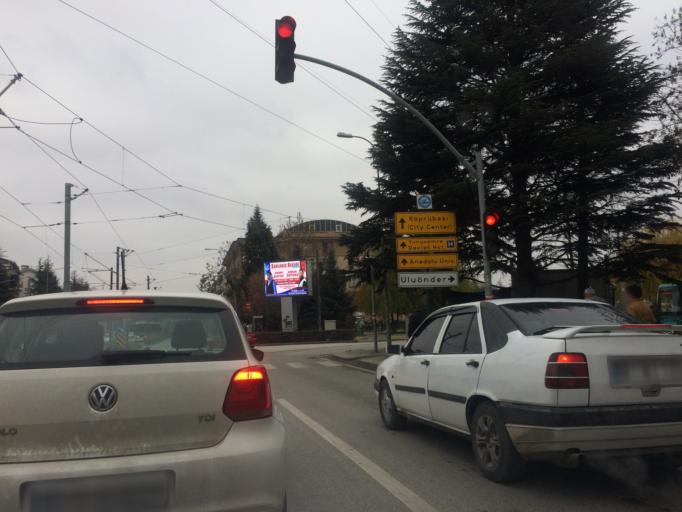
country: TR
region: Eskisehir
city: Eskisehir
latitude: 39.7900
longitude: 30.4847
